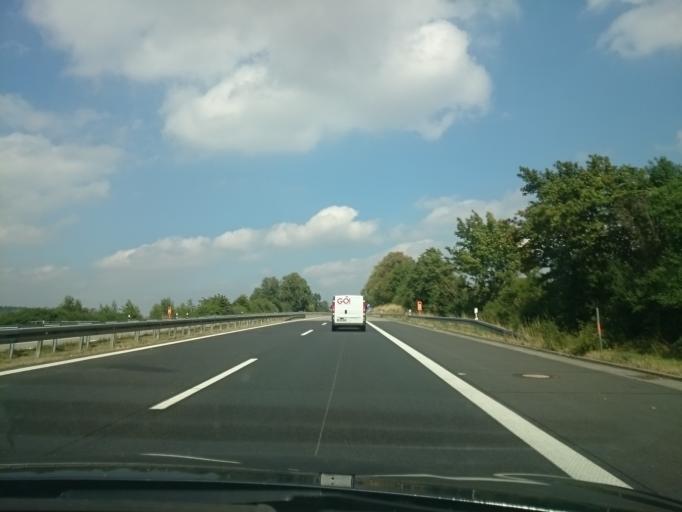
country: DE
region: Brandenburg
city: Althuttendorf
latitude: 53.0776
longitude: 13.8457
